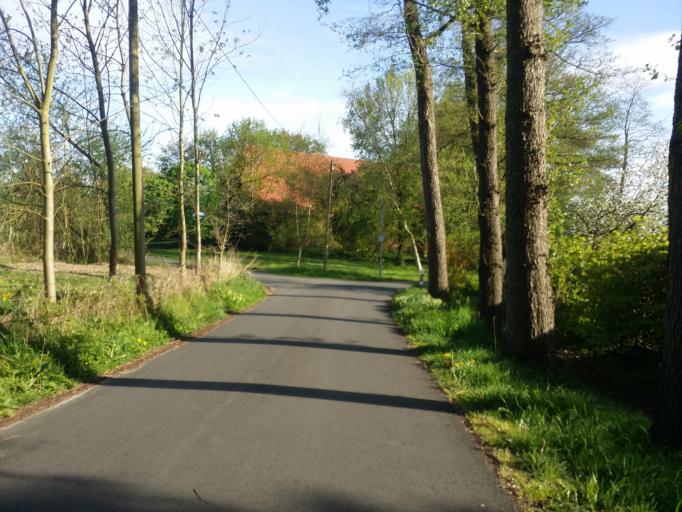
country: DE
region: Lower Saxony
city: Ritterhude
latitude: 53.1573
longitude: 8.7798
